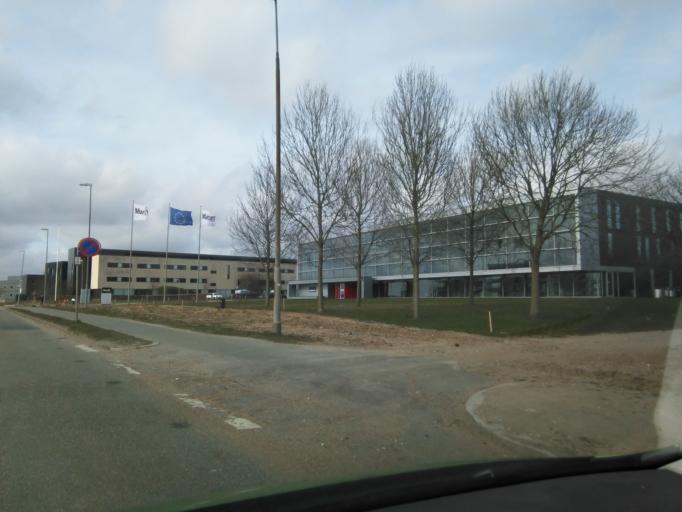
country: DK
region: Central Jutland
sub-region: Arhus Kommune
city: Arhus
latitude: 56.1877
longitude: 10.1880
